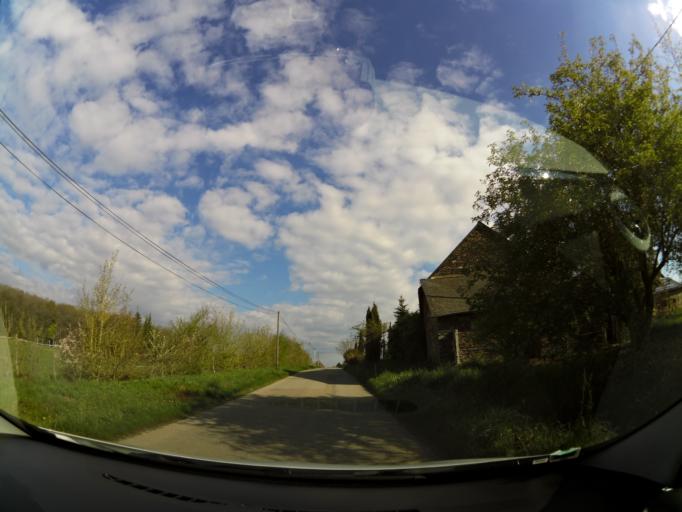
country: FR
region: Brittany
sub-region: Departement d'Ille-et-Vilaine
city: Laille
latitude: 47.9568
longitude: -1.7017
